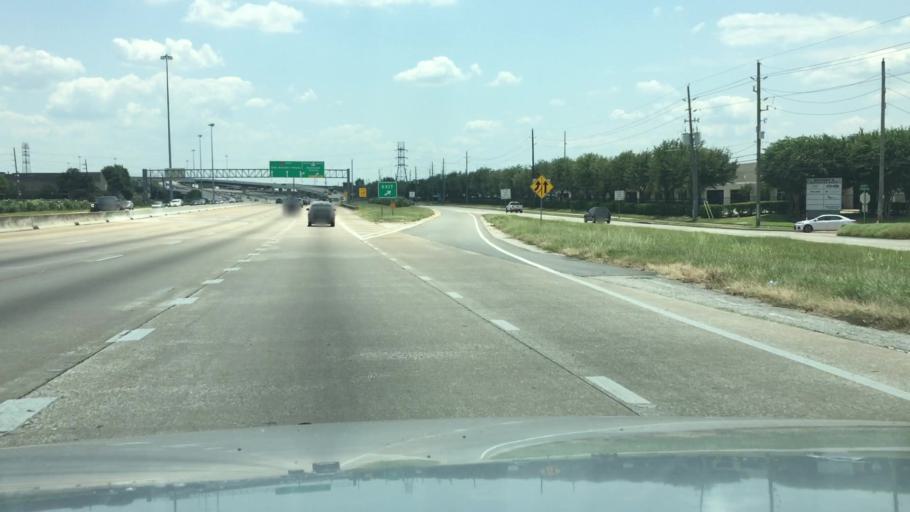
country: US
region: Texas
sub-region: Fort Bend County
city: Meadows Place
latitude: 29.6715
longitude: -95.5605
